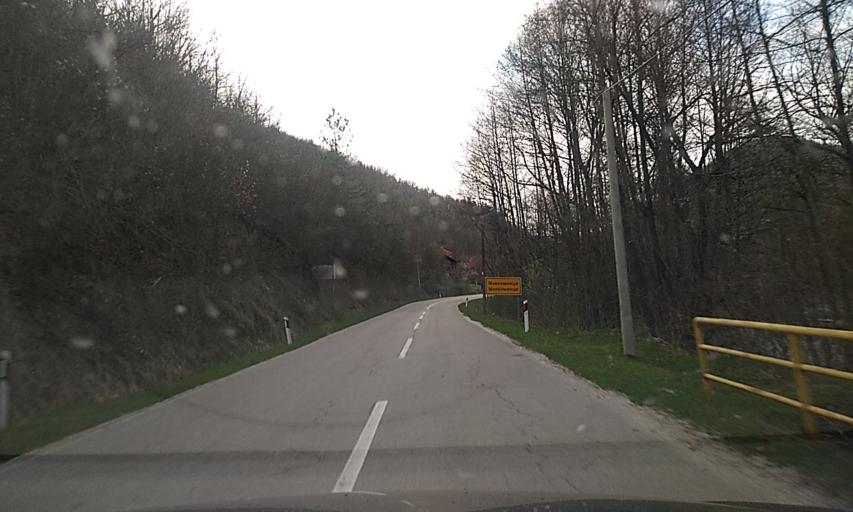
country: RS
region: Central Serbia
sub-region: Pcinjski Okrug
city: Bosilegrad
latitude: 42.4458
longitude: 22.5017
